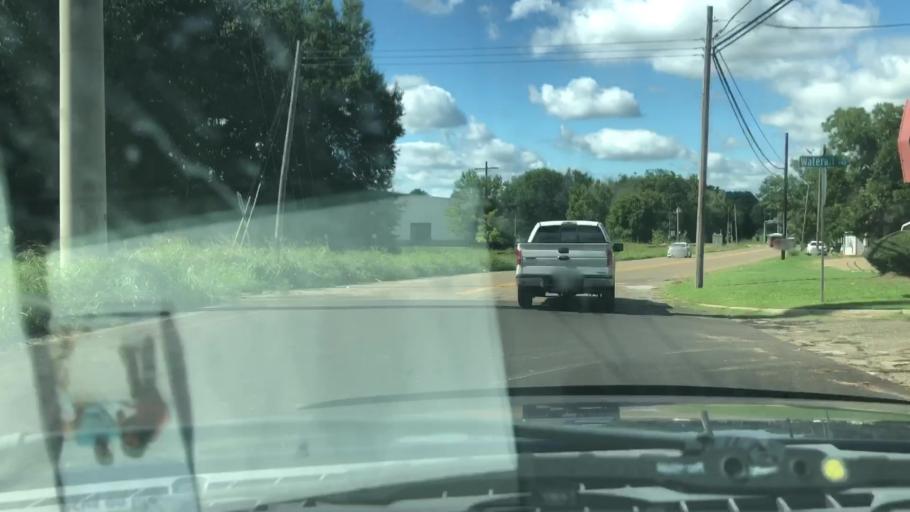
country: US
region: Texas
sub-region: Bowie County
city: Texarkana
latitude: 33.4194
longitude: -94.0589
